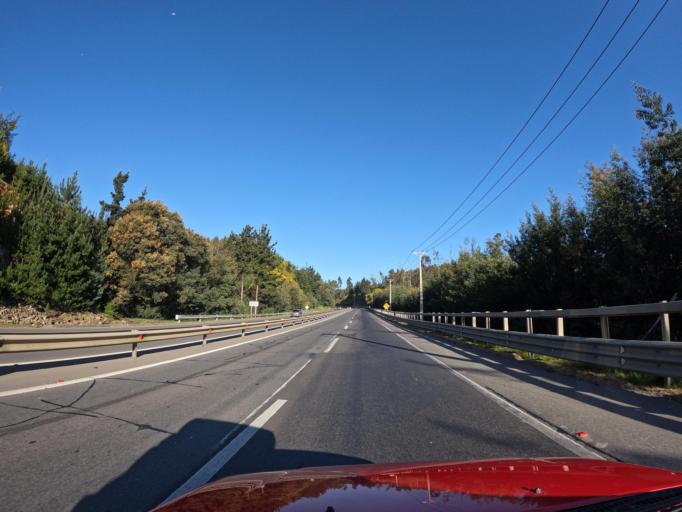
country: CL
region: Biobio
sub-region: Provincia de Concepcion
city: Penco
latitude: -36.7587
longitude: -72.9769
